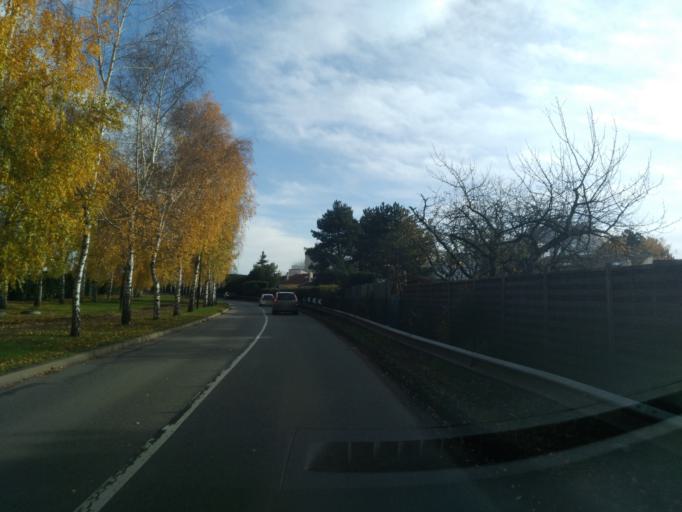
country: FR
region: Ile-de-France
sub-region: Departement des Yvelines
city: Plaisir
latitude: 48.8213
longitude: 1.9678
